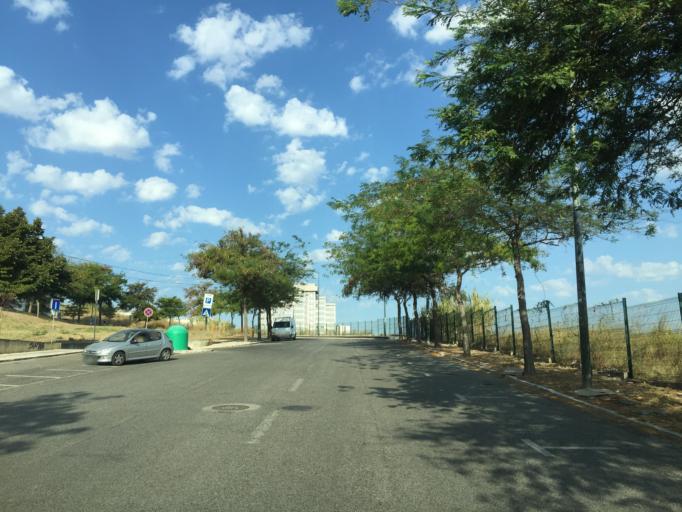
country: PT
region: Lisbon
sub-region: Lisbon
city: Lisbon
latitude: 38.7443
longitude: -9.1277
